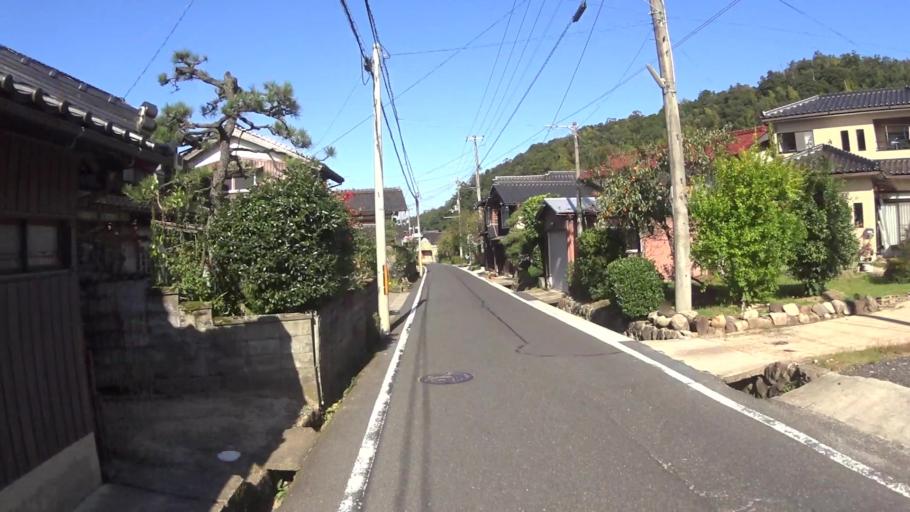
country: JP
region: Kyoto
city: Miyazu
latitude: 35.6555
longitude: 135.1152
